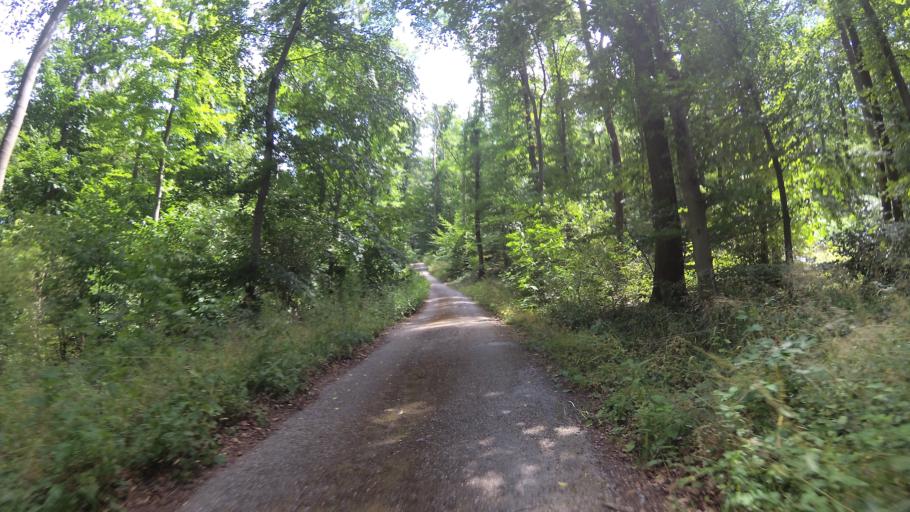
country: DE
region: Baden-Wuerttemberg
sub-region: Regierungsbezirk Stuttgart
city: Neckarsulm
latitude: 49.1984
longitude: 9.2527
